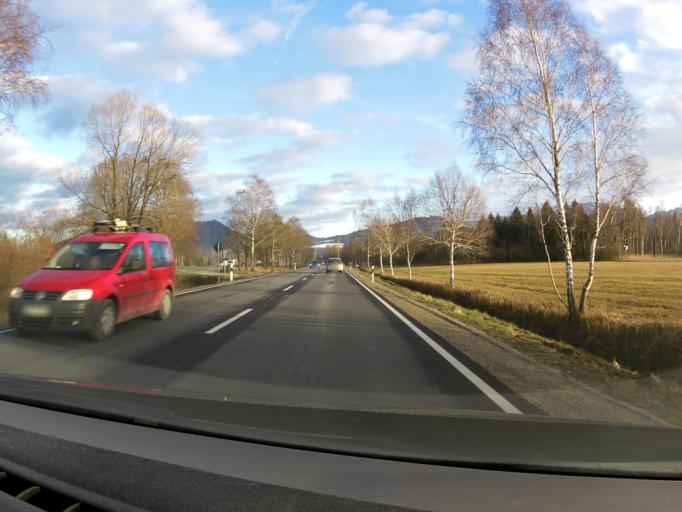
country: DE
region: Bavaria
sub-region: Upper Bavaria
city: Penzberg
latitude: 47.7244
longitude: 11.3832
